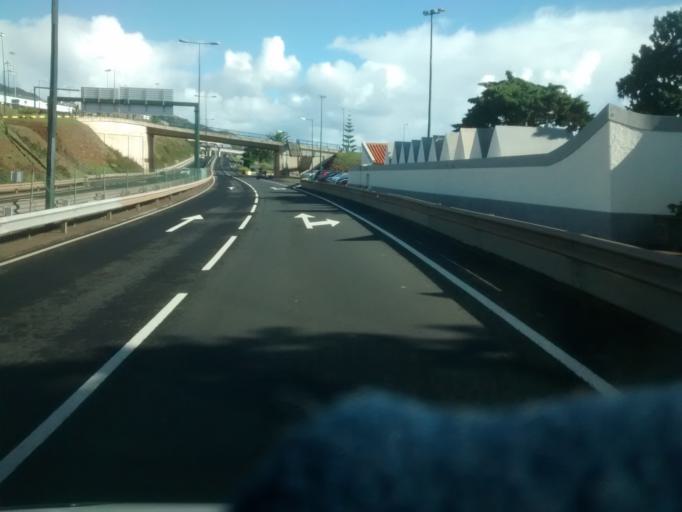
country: PT
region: Madeira
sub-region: Machico
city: Machico
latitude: 32.6919
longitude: -16.7746
